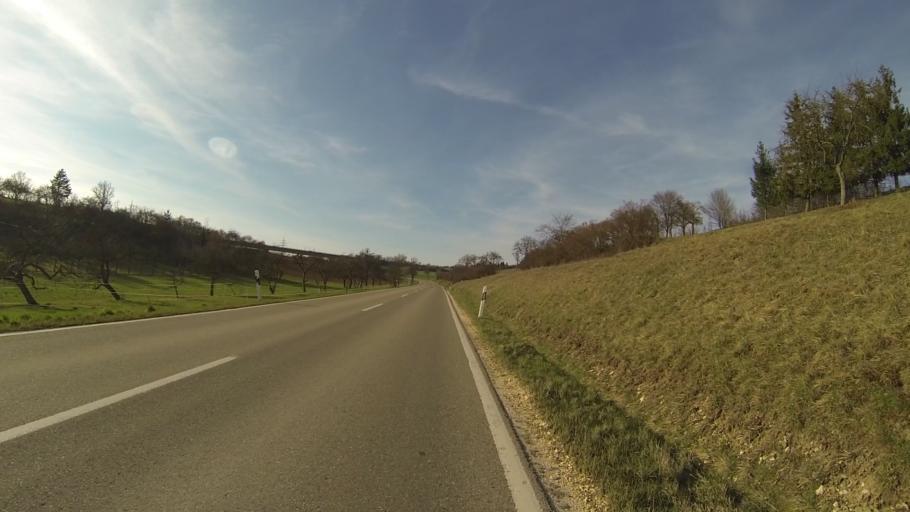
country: DE
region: Baden-Wuerttemberg
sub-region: Regierungsbezirk Stuttgart
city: Herbrechtingen
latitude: 48.6020
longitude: 10.2017
